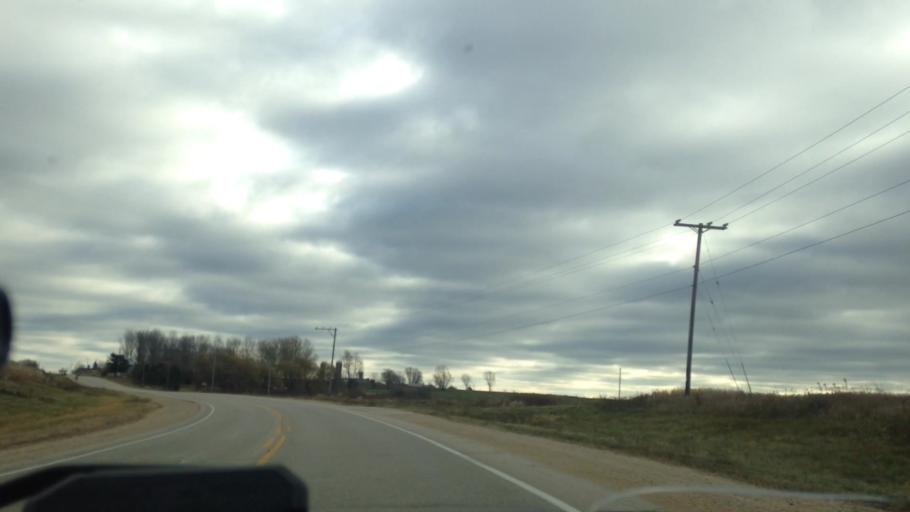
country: US
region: Wisconsin
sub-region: Dodge County
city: Theresa
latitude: 43.4214
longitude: -88.4087
